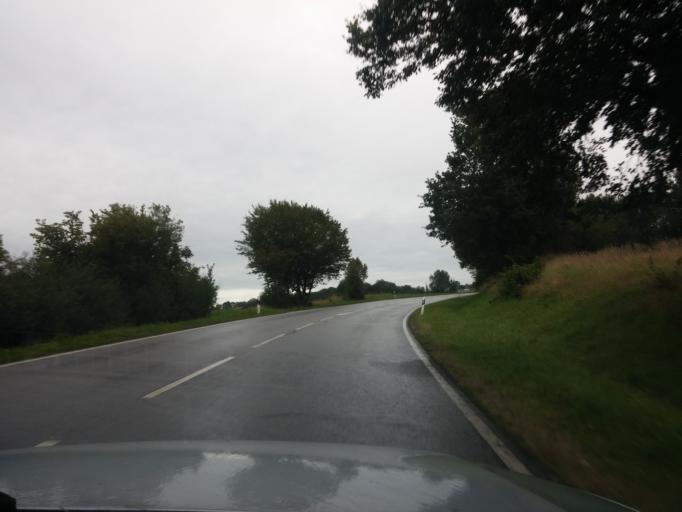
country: DE
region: Bavaria
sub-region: Upper Bavaria
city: Reichertshausen
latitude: 48.4628
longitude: 11.5135
